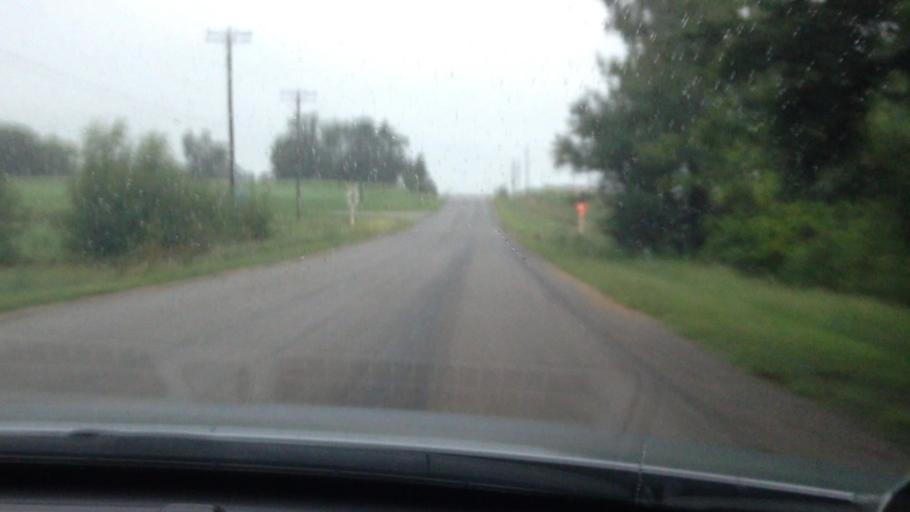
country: US
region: Kansas
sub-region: Brown County
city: Hiawatha
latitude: 39.8473
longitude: -95.5459
